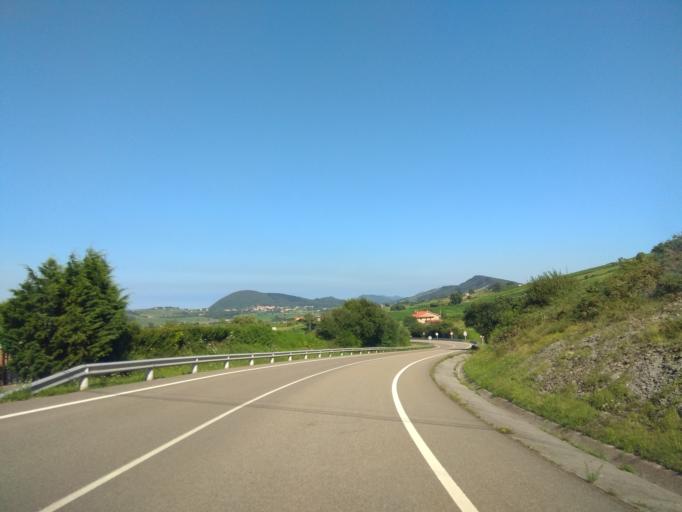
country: ES
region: Cantabria
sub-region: Provincia de Cantabria
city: Bareyo
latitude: 43.4735
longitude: -3.6149
